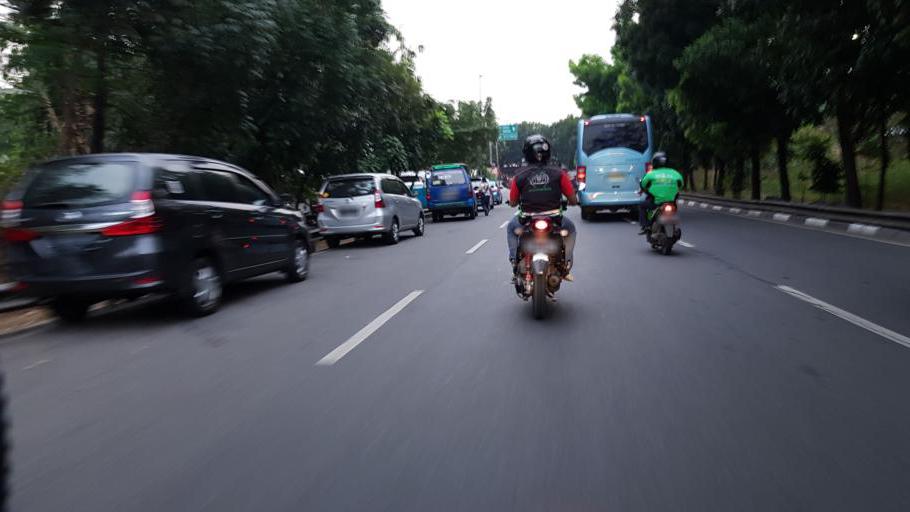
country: ID
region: Jakarta Raya
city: Jakarta
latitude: -6.3072
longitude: 106.8825
